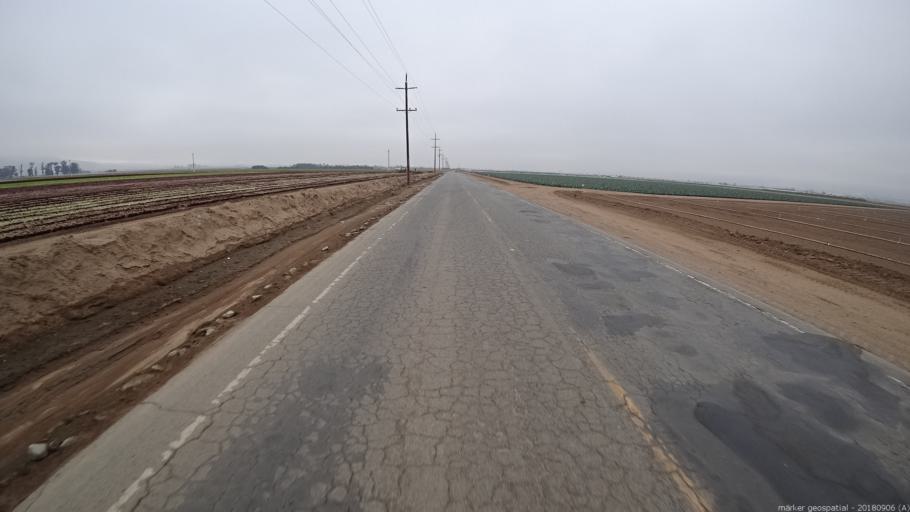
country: US
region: California
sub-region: Monterey County
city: Salinas
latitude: 36.6533
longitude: -121.5838
